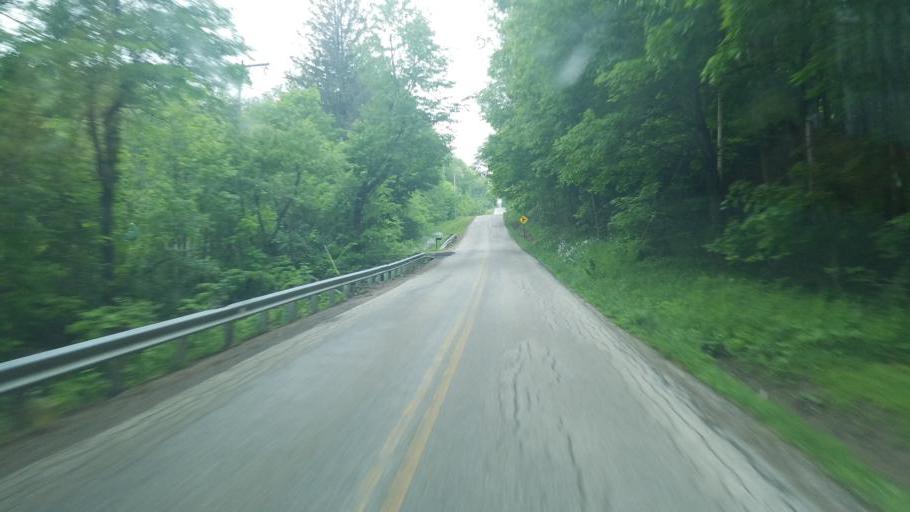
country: US
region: Ohio
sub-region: Sandusky County
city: Bellville
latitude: 40.6568
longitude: -82.4726
